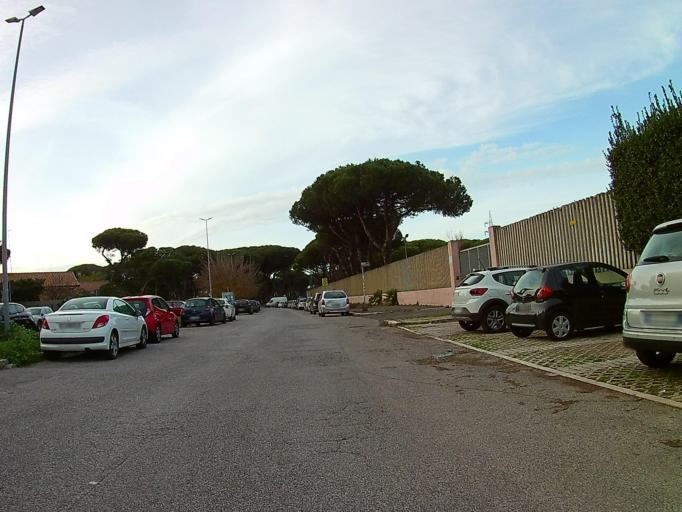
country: IT
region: Latium
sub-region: Citta metropolitana di Roma Capitale
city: Lido di Ostia
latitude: 41.7409
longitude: 12.2829
